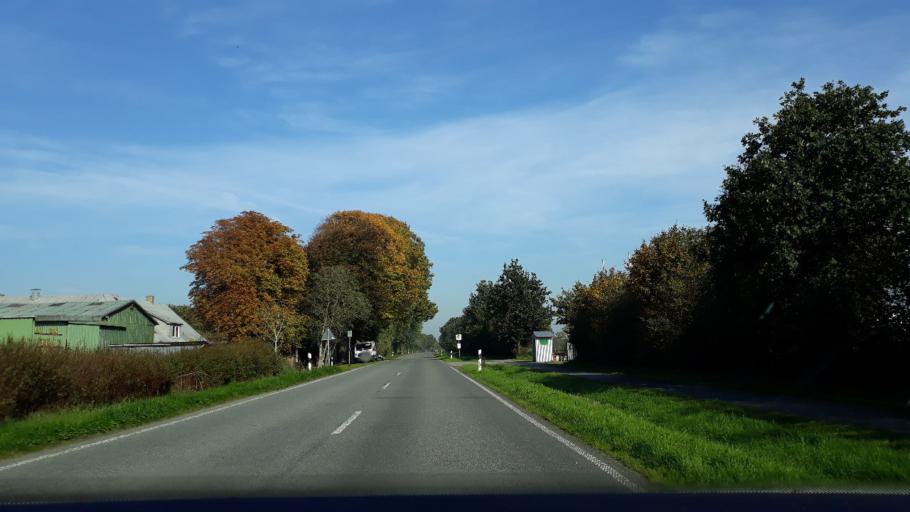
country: DE
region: Schleswig-Holstein
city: Gross Rheide
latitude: 54.4300
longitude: 9.4140
